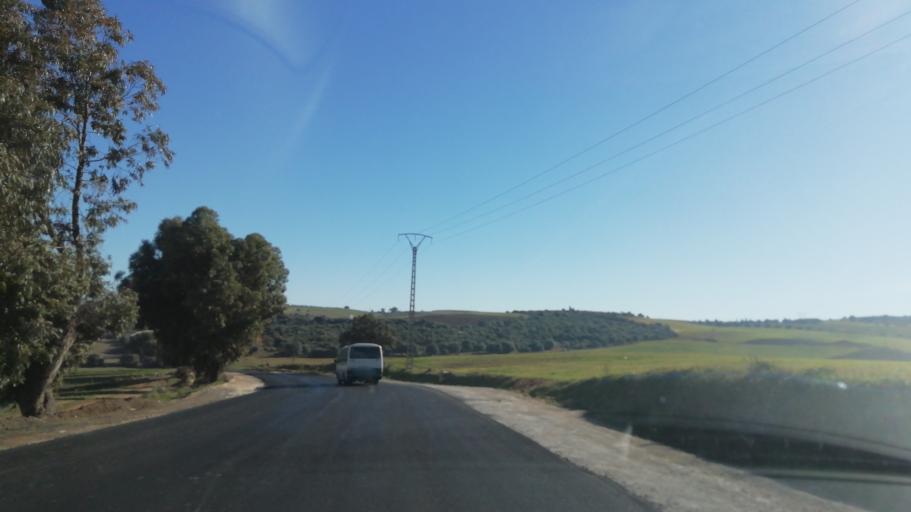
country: DZ
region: Relizane
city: Smala
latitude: 35.6699
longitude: 0.8061
